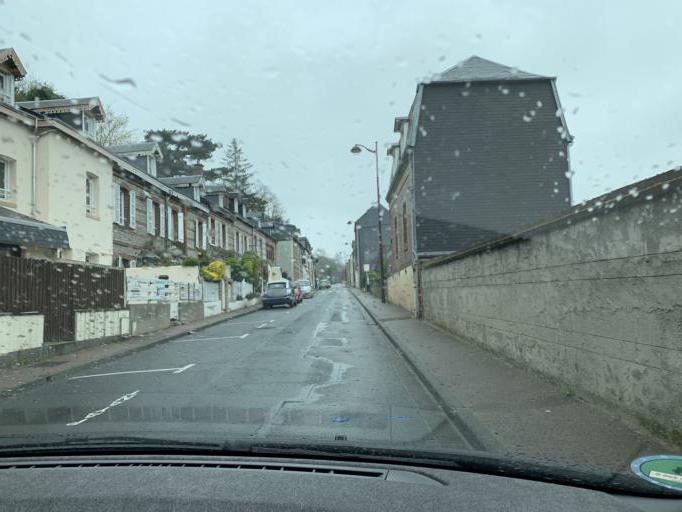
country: FR
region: Haute-Normandie
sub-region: Departement de la Seine-Maritime
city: Etretat
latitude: 49.7084
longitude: 0.2122
